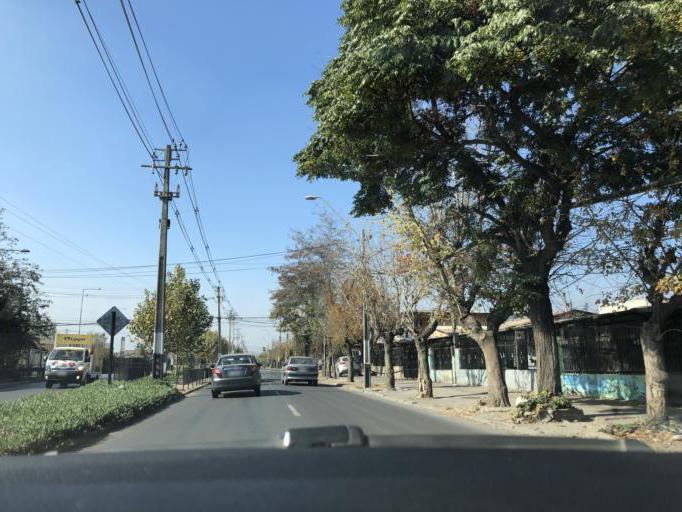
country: CL
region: Santiago Metropolitan
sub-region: Provincia de Cordillera
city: Puente Alto
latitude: -33.6048
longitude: -70.5918
